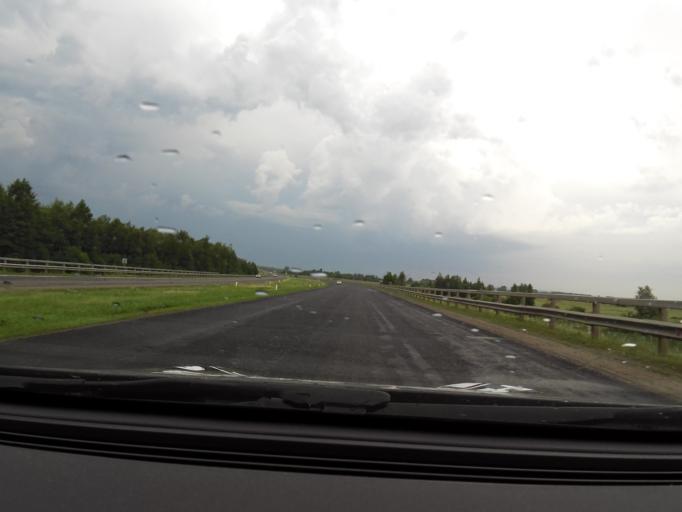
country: RU
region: Bashkortostan
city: Asanovo
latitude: 54.9641
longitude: 55.5838
